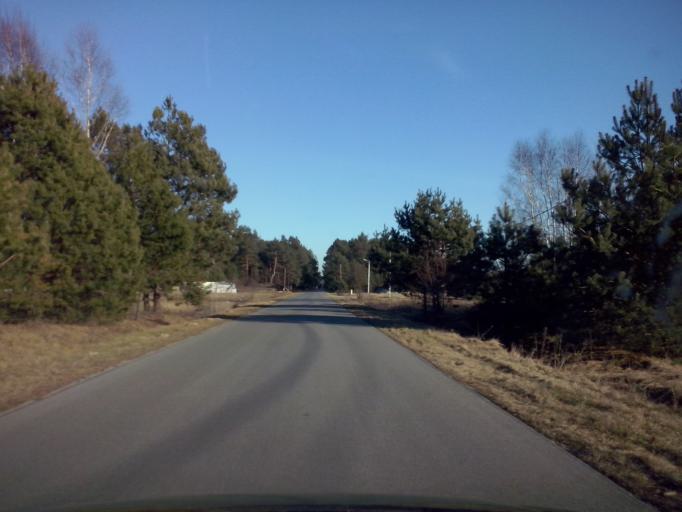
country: PL
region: Subcarpathian Voivodeship
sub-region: Powiat nizanski
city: Harasiuki
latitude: 50.5233
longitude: 22.4682
